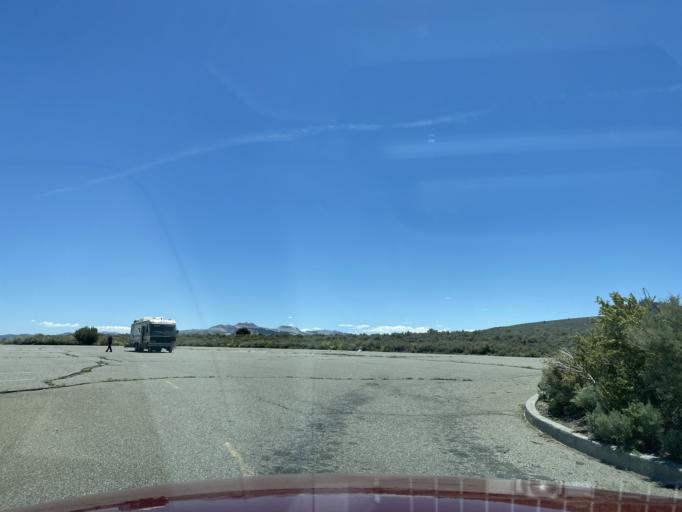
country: US
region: California
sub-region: Mono County
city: Bridgeport
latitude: 37.9661
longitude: -119.1217
